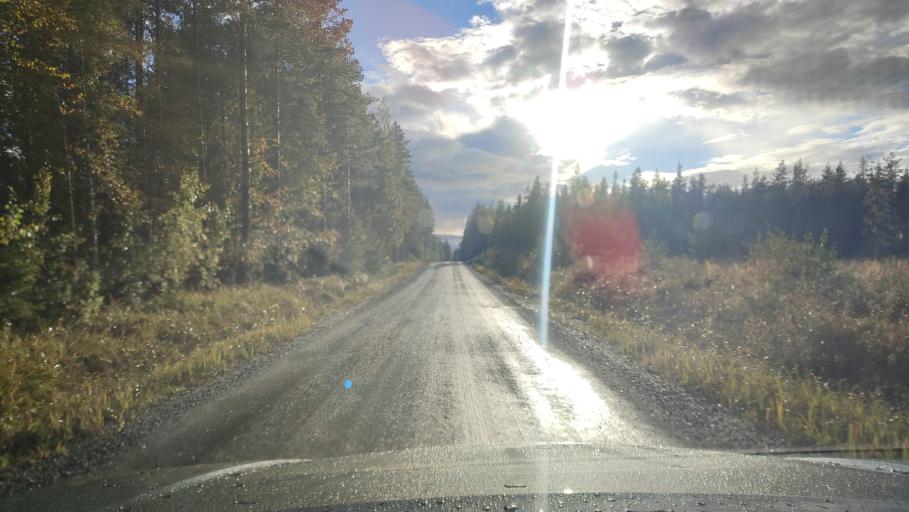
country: FI
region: Ostrobothnia
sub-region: Sydosterbotten
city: Kristinestad
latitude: 62.3078
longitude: 21.5401
